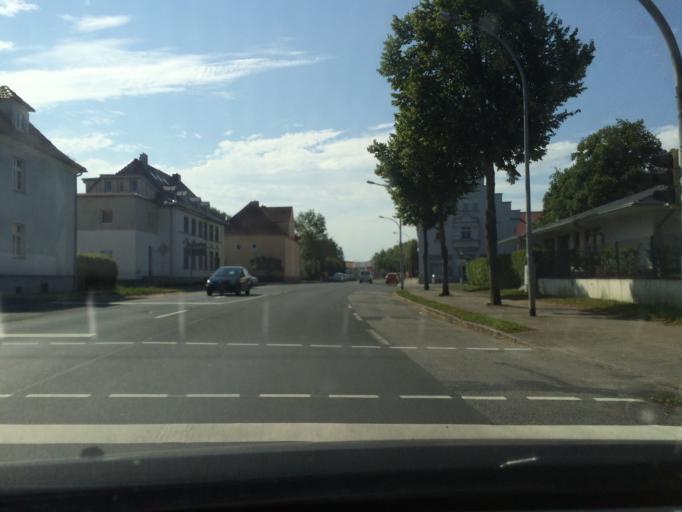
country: DE
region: Mecklenburg-Vorpommern
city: Stralsund
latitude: 54.3050
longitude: 13.0909
